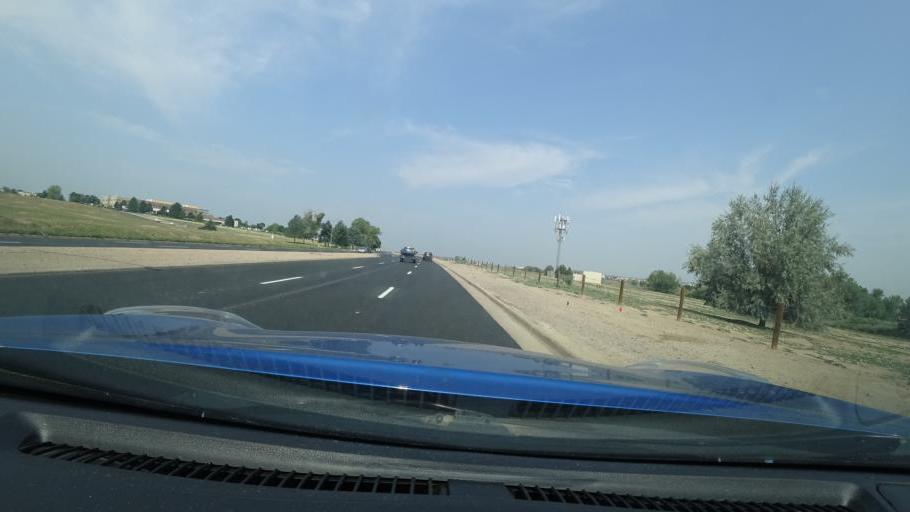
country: US
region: Colorado
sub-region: Adams County
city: Aurora
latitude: 39.7049
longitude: -104.7786
